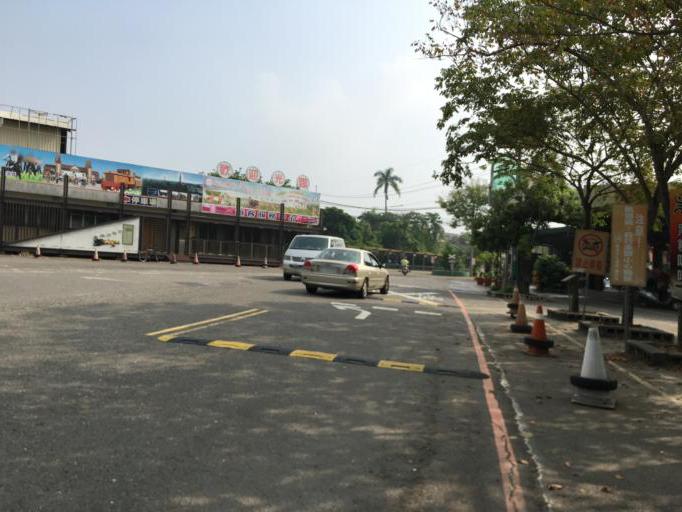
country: TW
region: Taiwan
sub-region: Chiayi
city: Taibao
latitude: 23.4790
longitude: 120.2995
